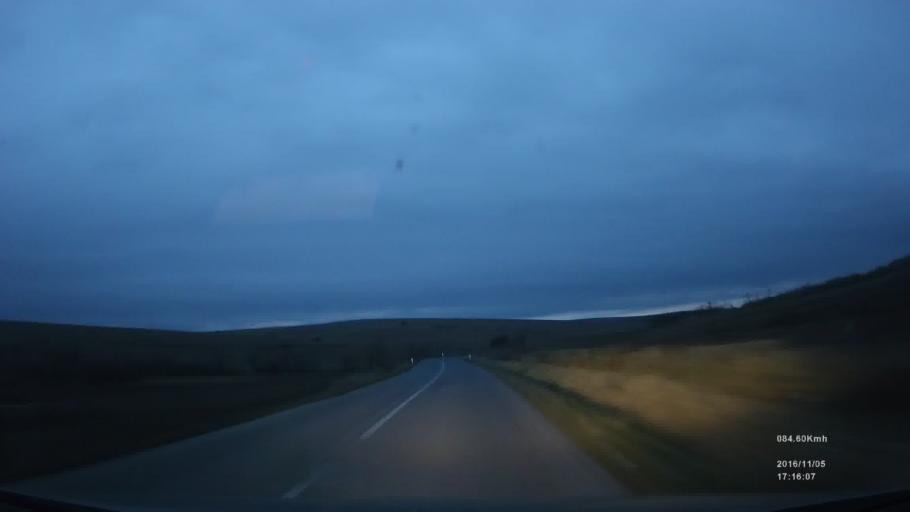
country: SK
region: Presovsky
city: Lubica
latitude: 49.0971
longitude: 20.4403
